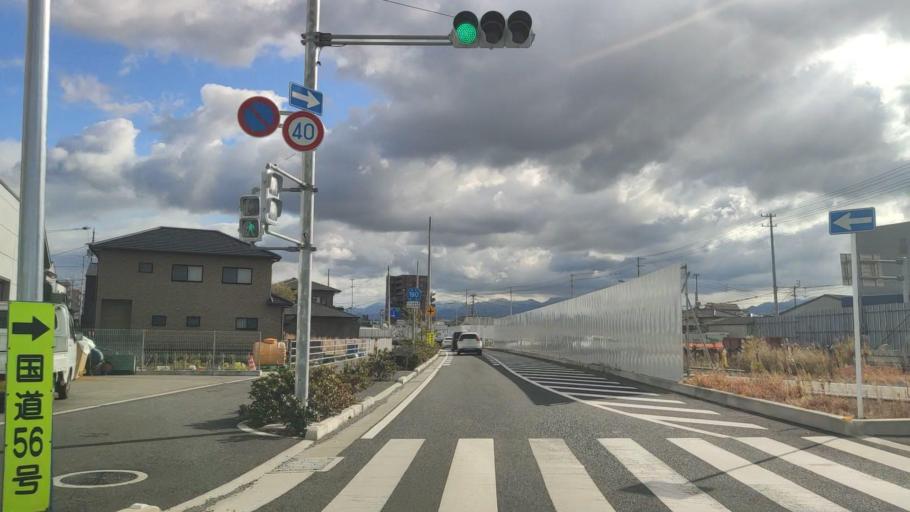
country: JP
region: Ehime
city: Masaki-cho
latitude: 33.8118
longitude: 132.7243
